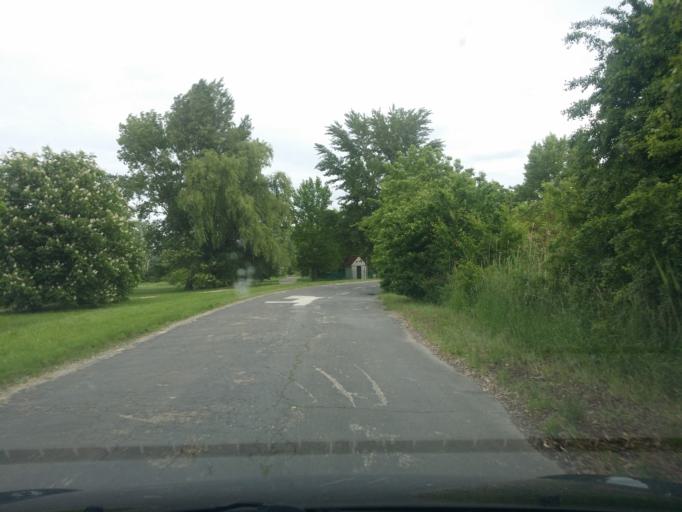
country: HU
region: Somogy
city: Balatonszabadi
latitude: 46.9367
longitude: 18.1389
